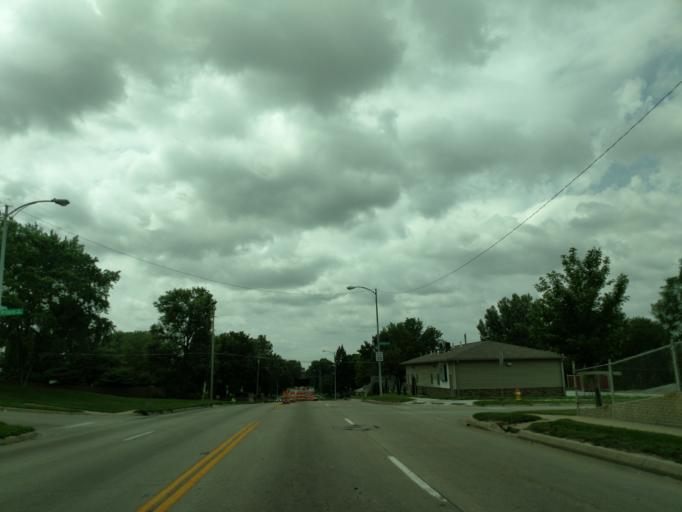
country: US
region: Nebraska
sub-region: Sarpy County
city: La Vista
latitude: 41.2095
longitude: -96.0047
